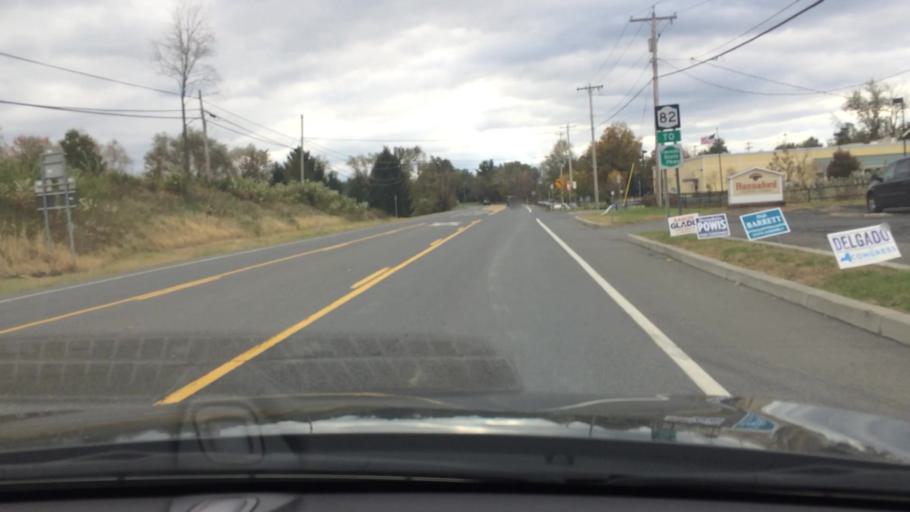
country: US
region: New York
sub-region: Columbia County
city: Oakdale
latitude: 42.1759
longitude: -73.7588
